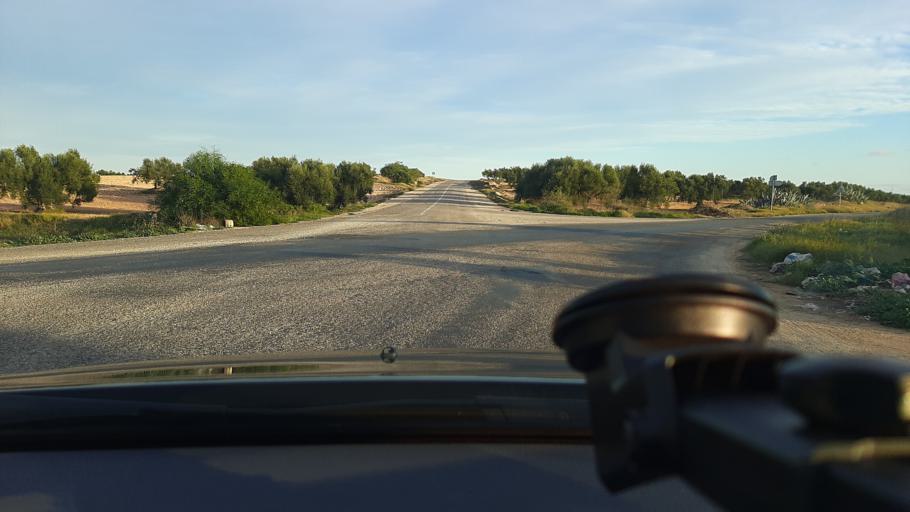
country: TN
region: Safaqis
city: Sfax
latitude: 34.9561
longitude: 10.5452
